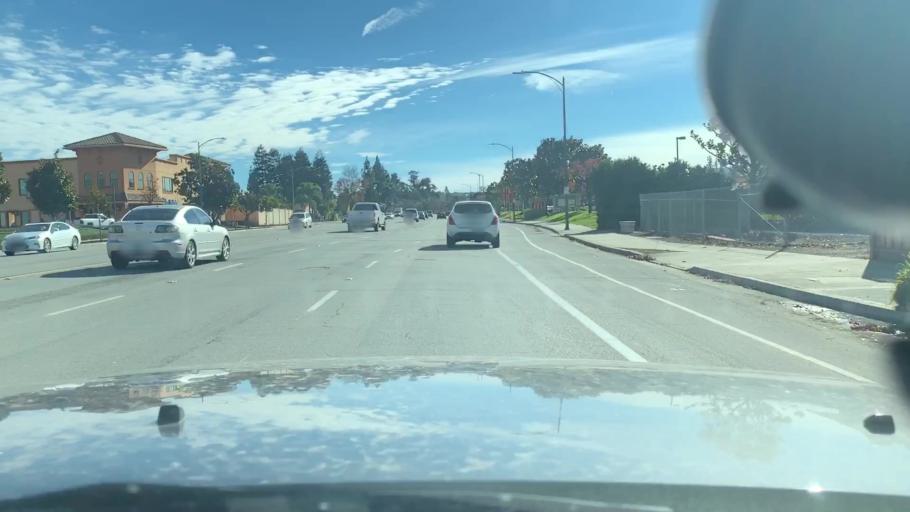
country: US
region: California
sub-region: Santa Clara County
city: Seven Trees
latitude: 37.3173
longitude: -121.7937
